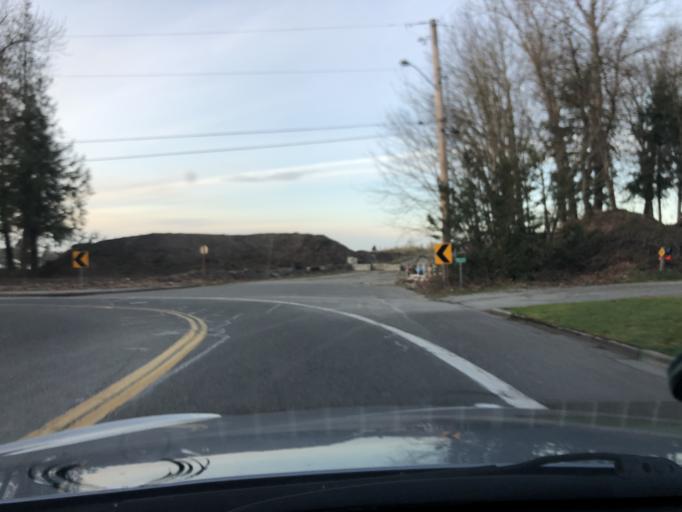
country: US
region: Washington
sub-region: King County
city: Auburn
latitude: 47.2935
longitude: -122.2081
